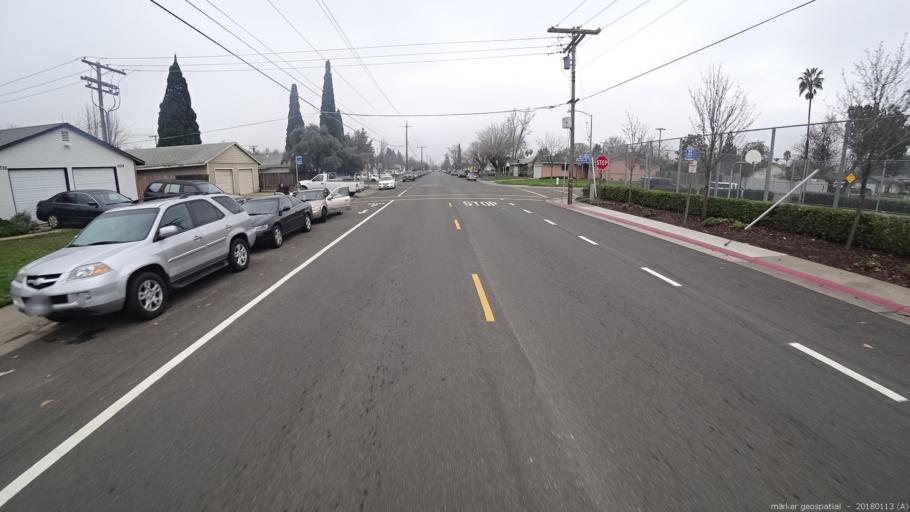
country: US
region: California
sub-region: Sacramento County
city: Rancho Cordova
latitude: 38.5786
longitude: -121.2985
